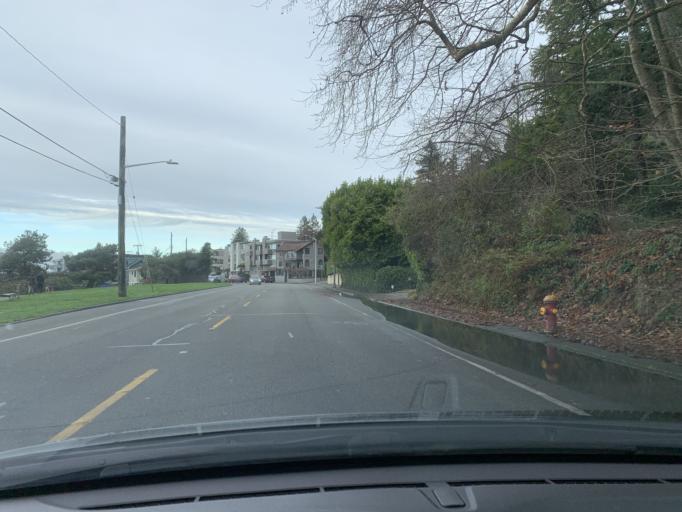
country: US
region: Washington
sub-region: King County
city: White Center
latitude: 47.5640
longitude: -122.4066
